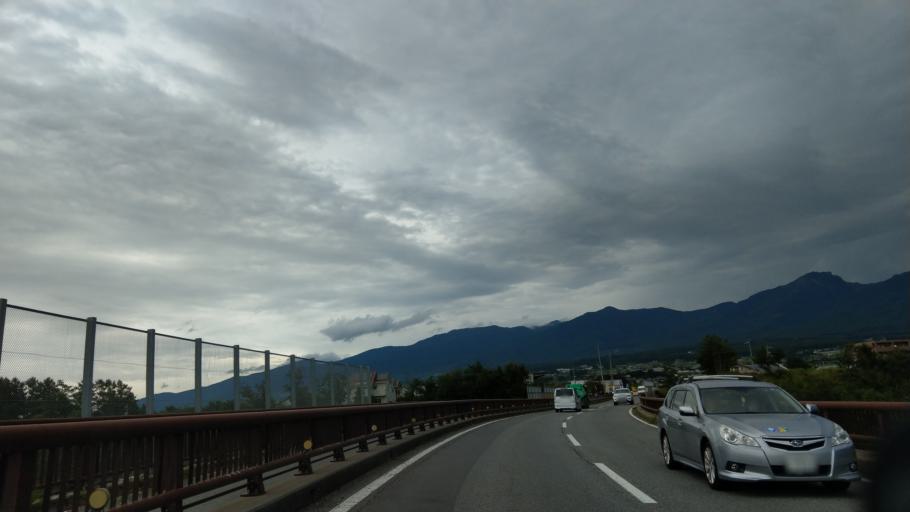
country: JP
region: Nagano
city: Komoro
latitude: 36.3078
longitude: 138.4564
